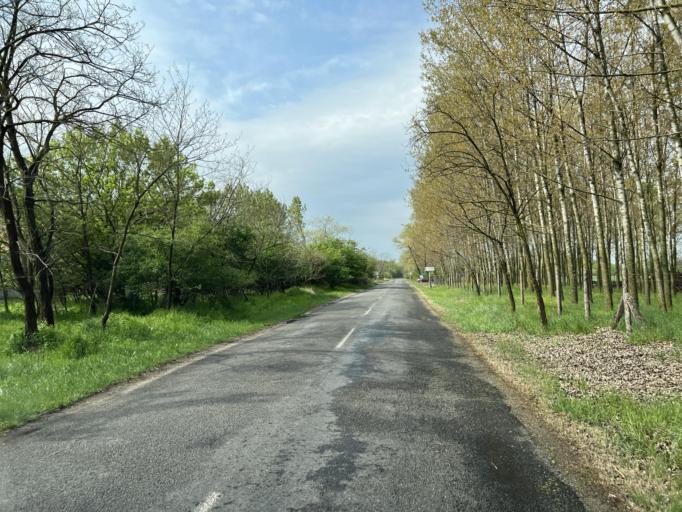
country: HU
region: Pest
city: Danszentmiklos
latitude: 47.1655
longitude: 19.5131
